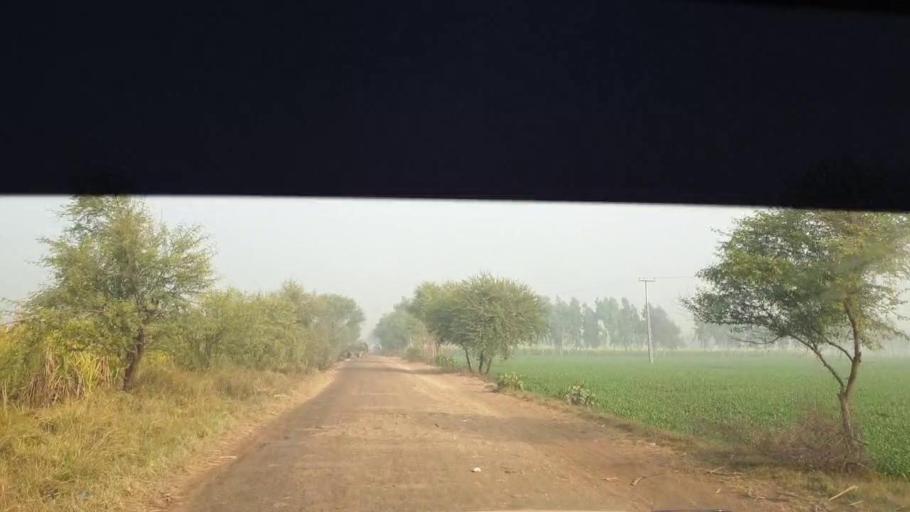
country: PK
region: Sindh
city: Berani
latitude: 25.7868
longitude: 68.7716
